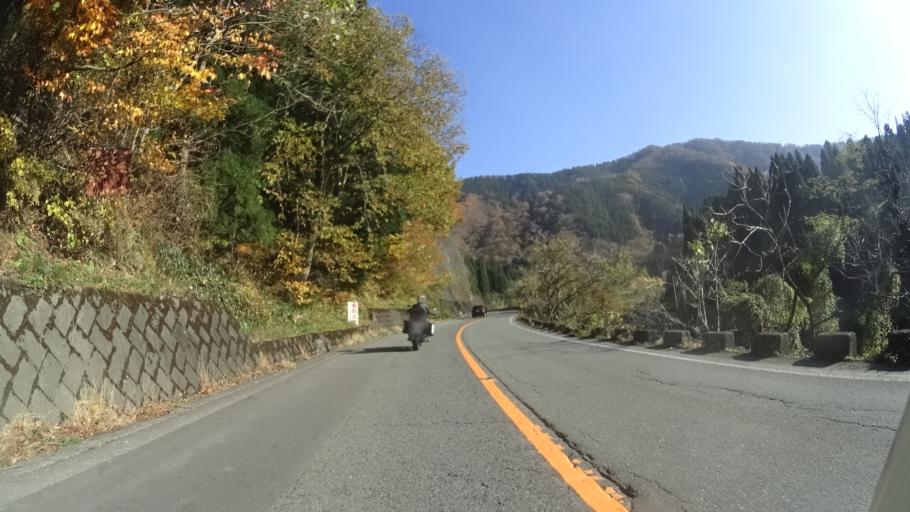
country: JP
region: Fukui
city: Ono
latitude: 35.9256
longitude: 136.6420
